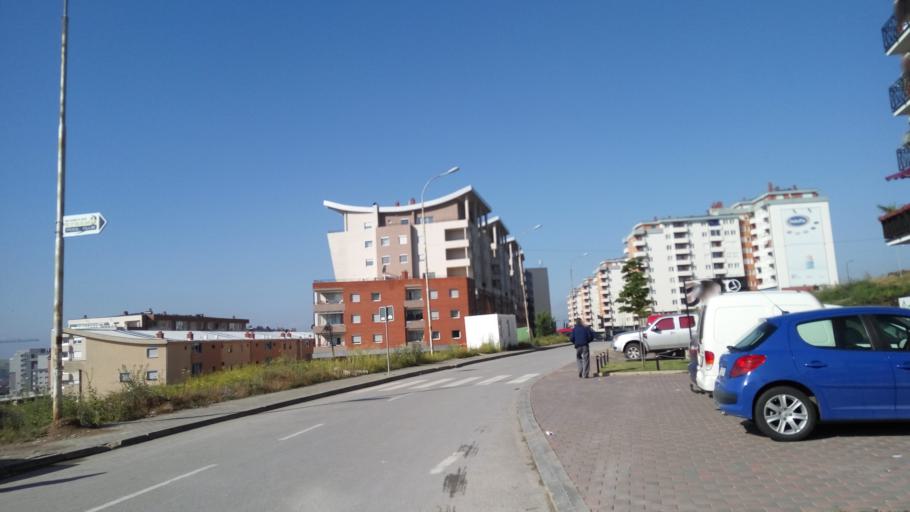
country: XK
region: Pristina
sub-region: Komuna e Prishtines
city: Pristina
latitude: 42.6594
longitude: 21.1492
